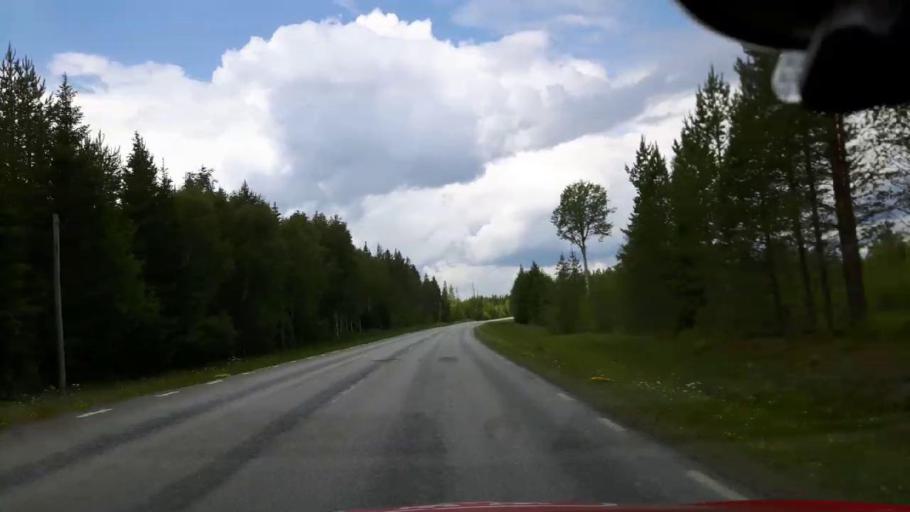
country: SE
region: Jaemtland
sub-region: Krokoms Kommun
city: Krokom
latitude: 63.3586
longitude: 14.4062
